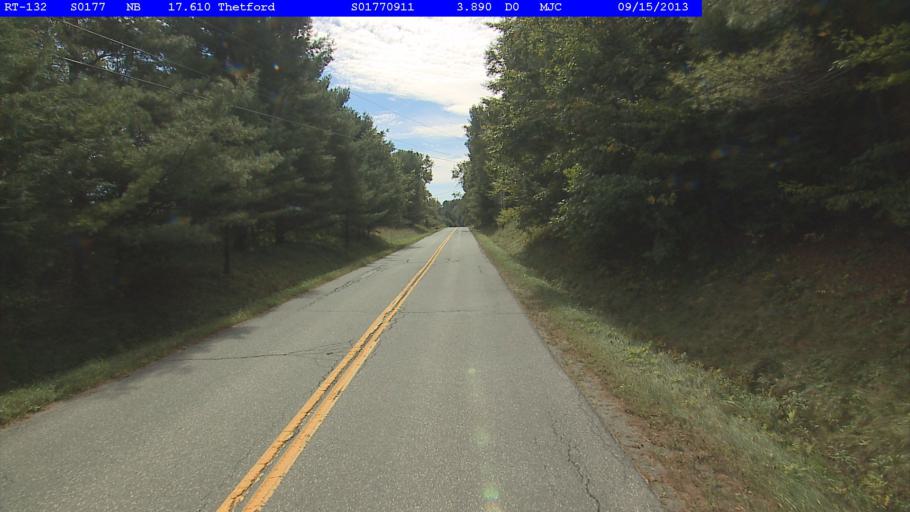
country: US
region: New Hampshire
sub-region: Grafton County
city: Hanover
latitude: 43.8036
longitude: -72.2676
